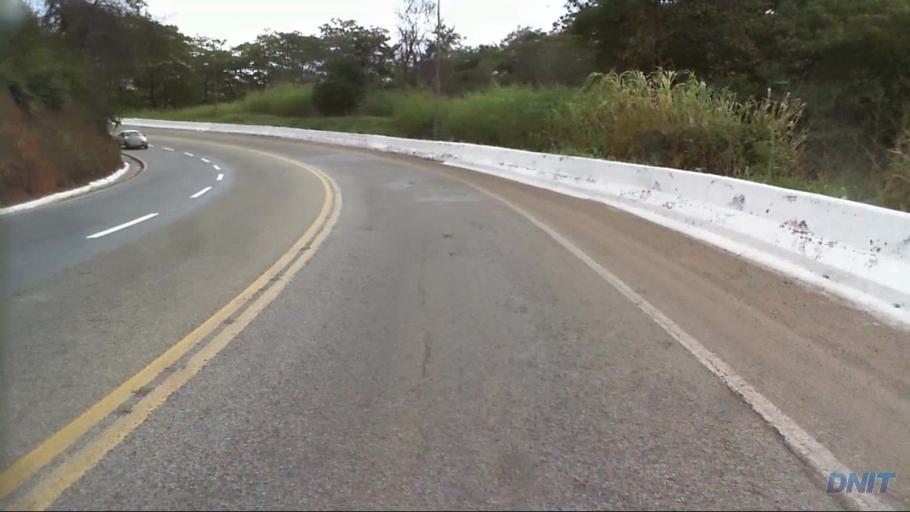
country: BR
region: Minas Gerais
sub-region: Caete
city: Caete
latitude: -19.7864
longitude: -43.7335
